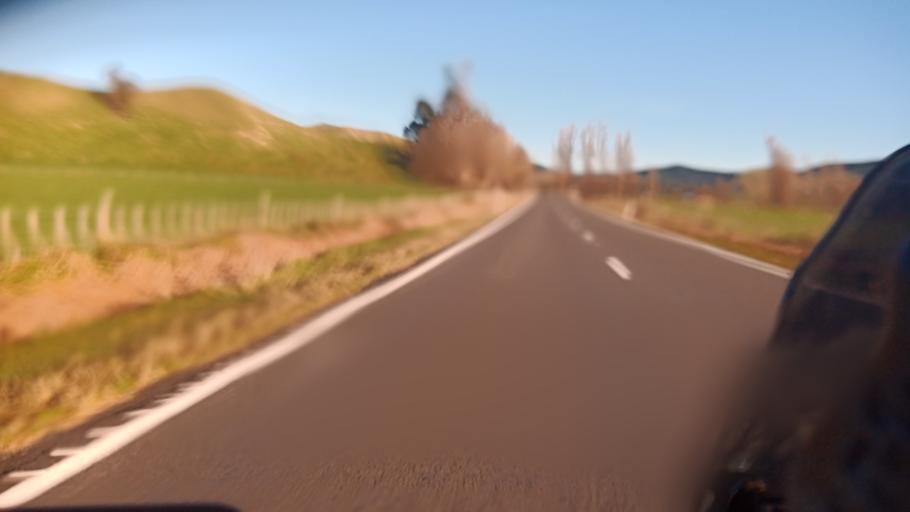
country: NZ
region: Hawke's Bay
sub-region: Wairoa District
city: Wairoa
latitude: -39.0167
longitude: 177.3674
